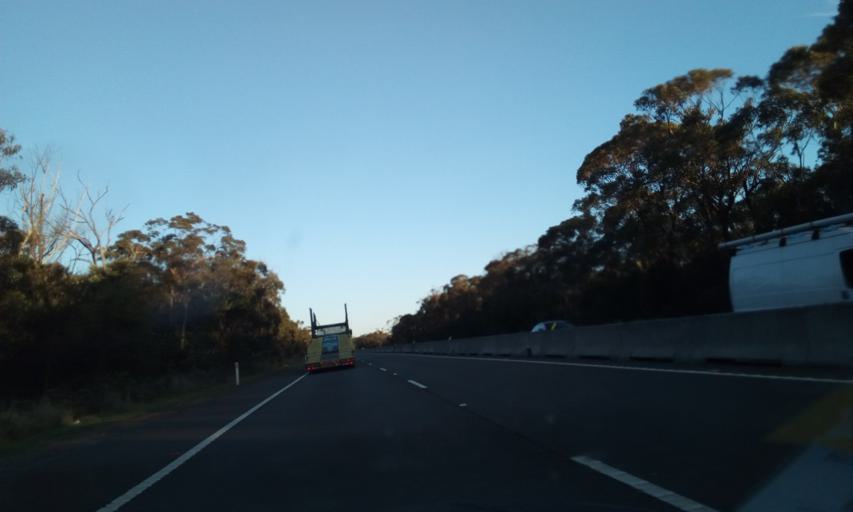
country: AU
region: New South Wales
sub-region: Wollongong
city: Mount Keira
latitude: -34.3383
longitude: 150.7864
